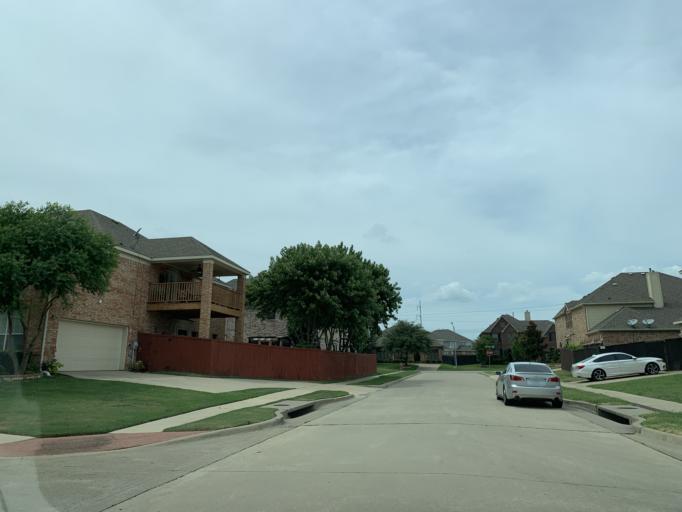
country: US
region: Texas
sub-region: Dallas County
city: Grand Prairie
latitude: 32.6531
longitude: -97.0373
